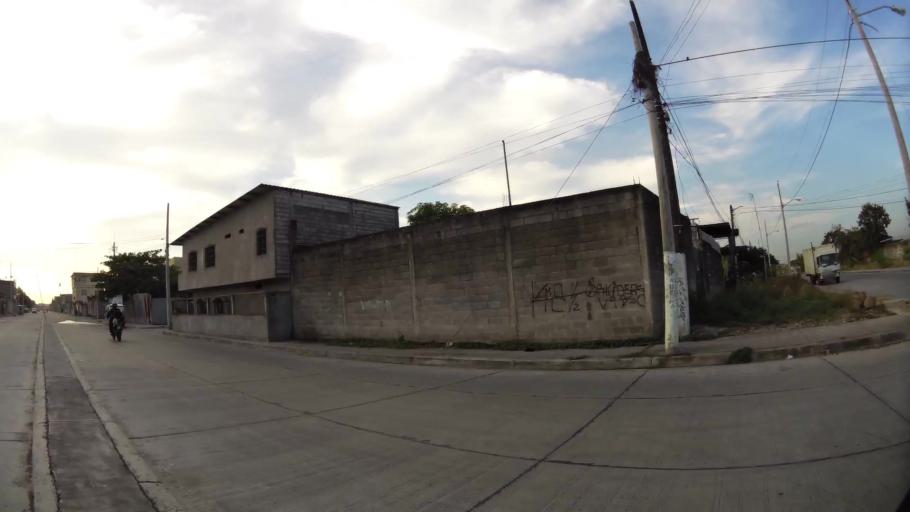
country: EC
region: Guayas
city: Eloy Alfaro
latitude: -2.0892
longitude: -79.9087
